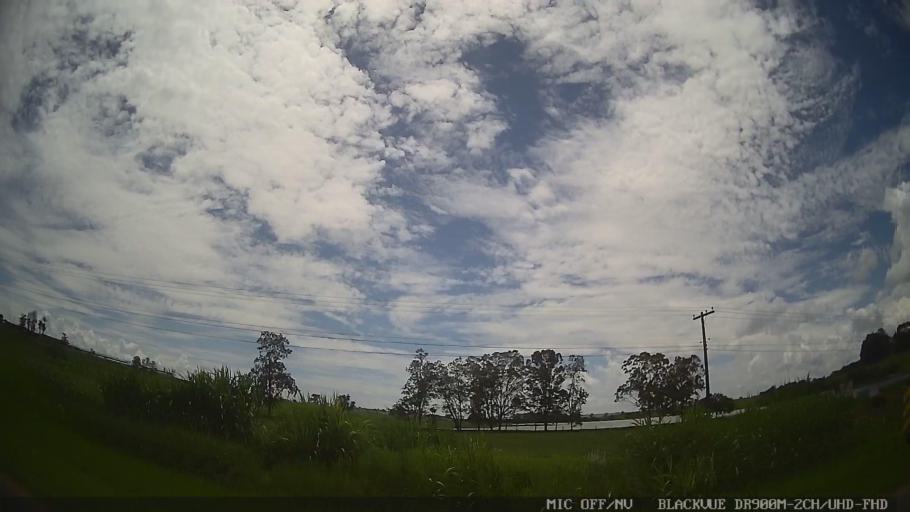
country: BR
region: Sao Paulo
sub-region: Conchas
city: Conchas
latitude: -23.0573
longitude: -47.9632
